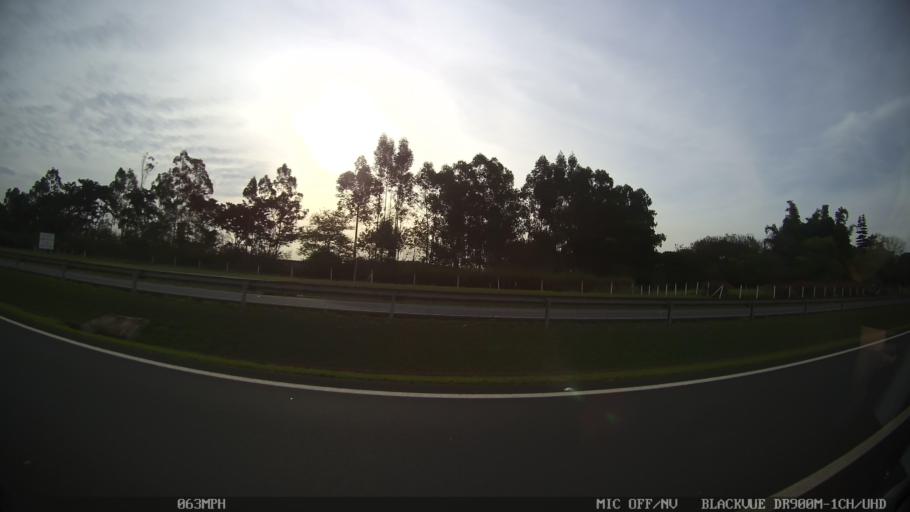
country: BR
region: Sao Paulo
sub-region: Iracemapolis
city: Iracemapolis
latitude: -22.6503
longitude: -47.5140
